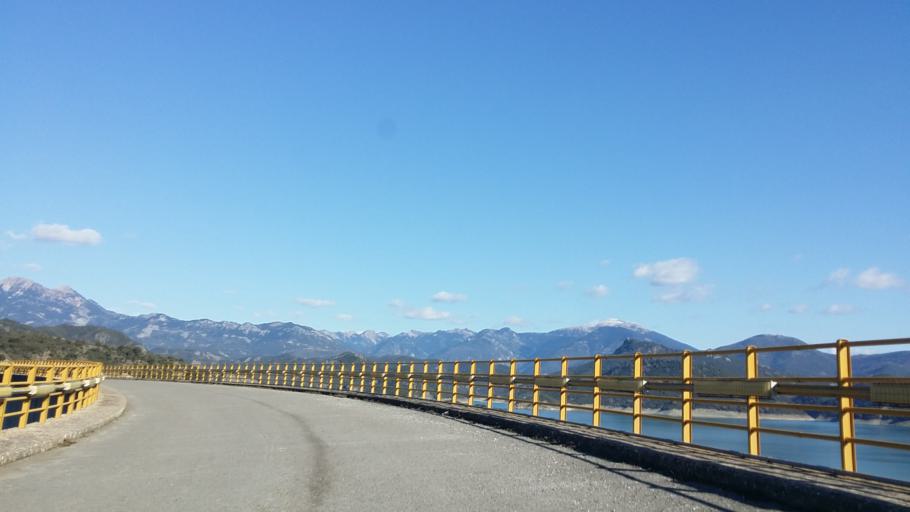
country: GR
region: Central Greece
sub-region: Nomos Evrytanias
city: Kerasochori
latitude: 38.9689
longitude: 21.4904
